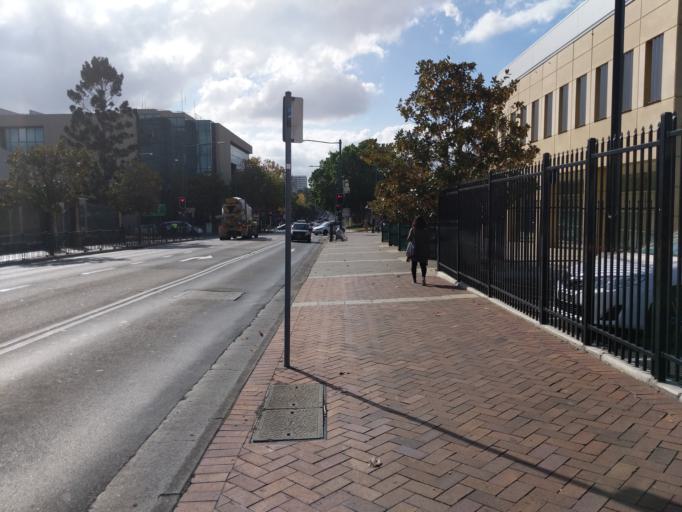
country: AU
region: New South Wales
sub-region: Fairfield
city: Liverpool
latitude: -33.9236
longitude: 150.9268
